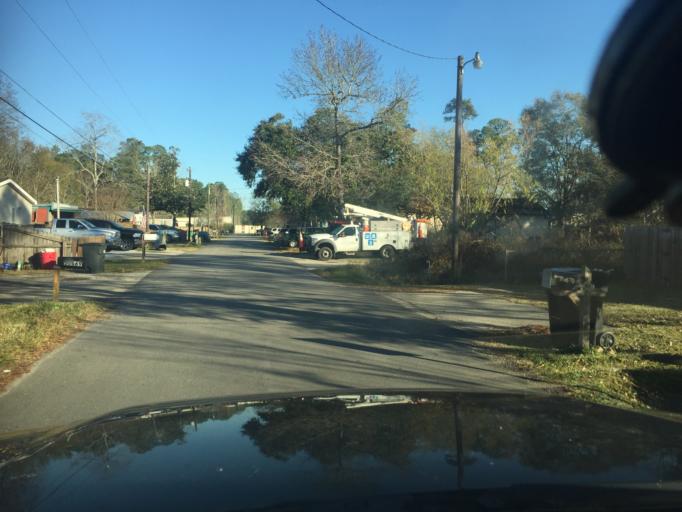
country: US
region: Louisiana
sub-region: Saint Tammany Parish
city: Slidell
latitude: 30.2534
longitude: -89.7645
